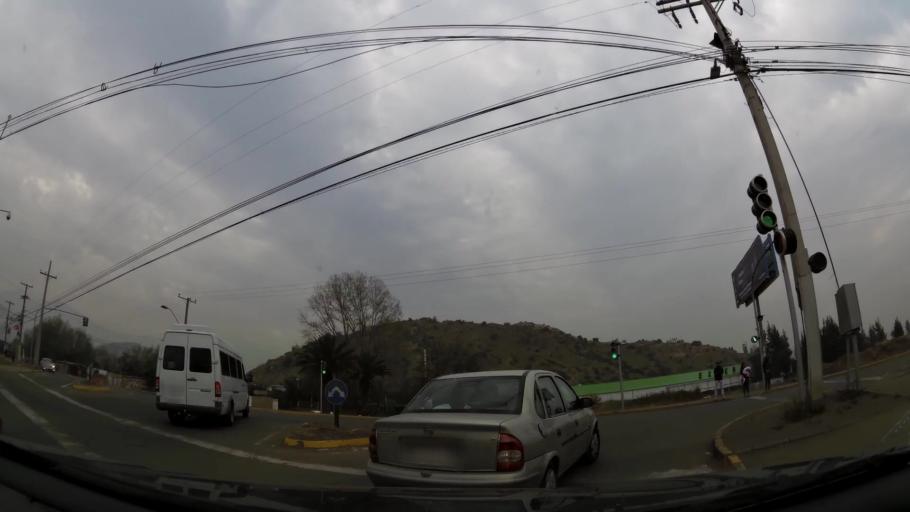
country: CL
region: Santiago Metropolitan
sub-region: Provincia de Chacabuco
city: Chicureo Abajo
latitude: -33.1921
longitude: -70.6636
